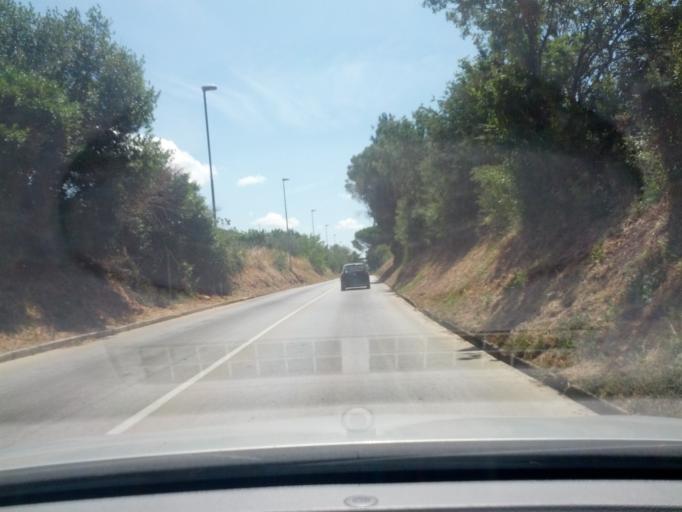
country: HR
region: Istarska
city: Fazana
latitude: 44.9132
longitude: 13.8186
